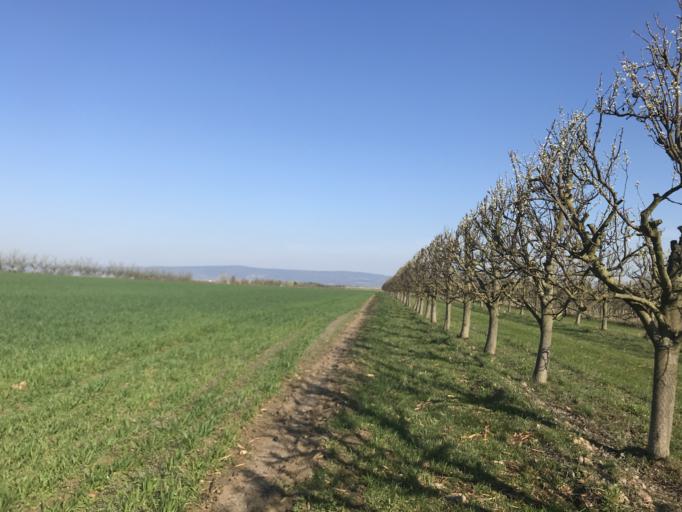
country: DE
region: Rheinland-Pfalz
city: Wackernheim
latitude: 49.9615
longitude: 8.1427
